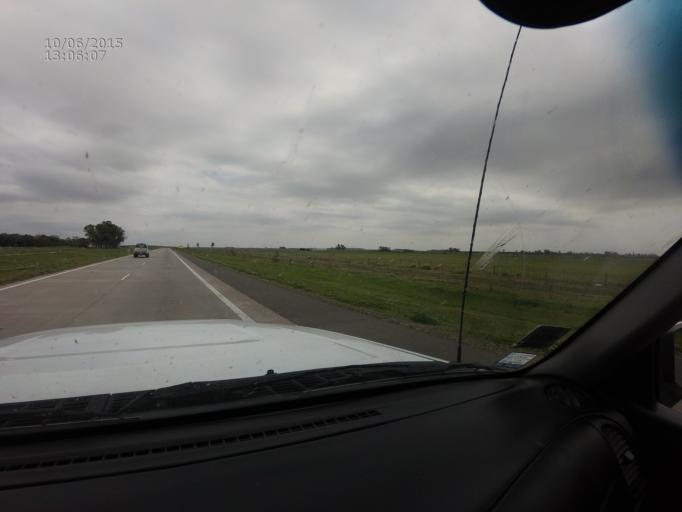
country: AR
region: Cordoba
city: General Roca
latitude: -32.7724
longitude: -61.8207
